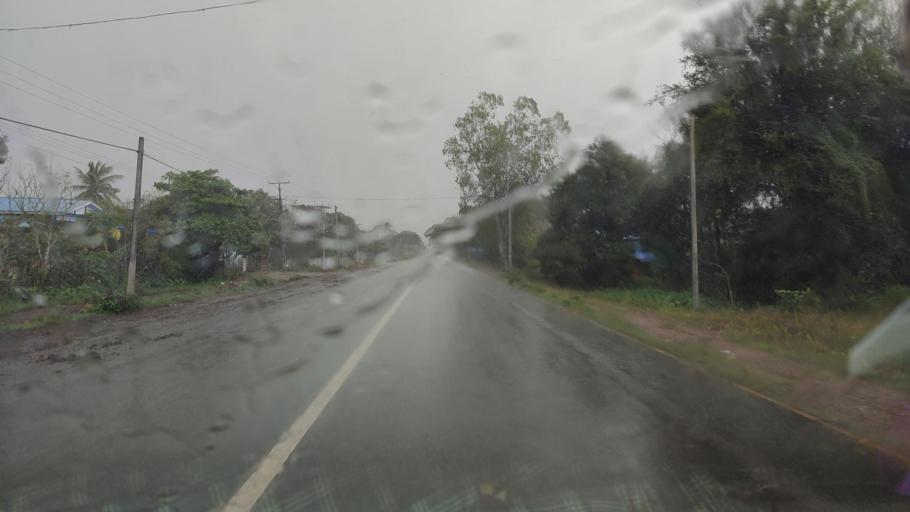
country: MM
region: Bago
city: Bago
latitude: 17.5734
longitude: 96.5520
